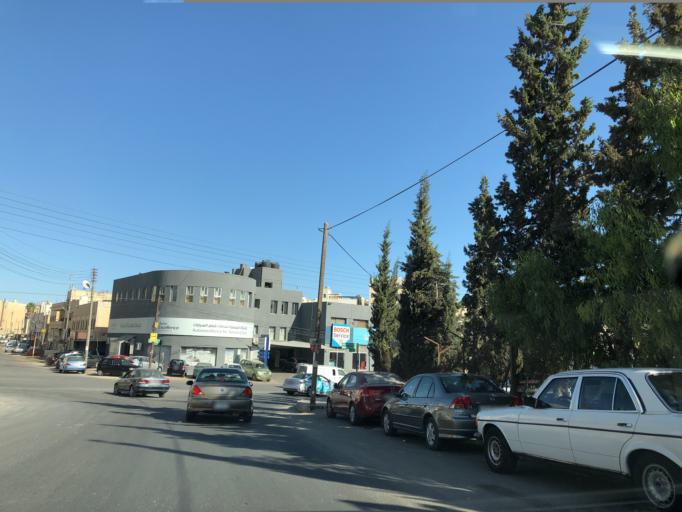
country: JO
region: Amman
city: Wadi as Sir
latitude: 31.9434
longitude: 35.8468
